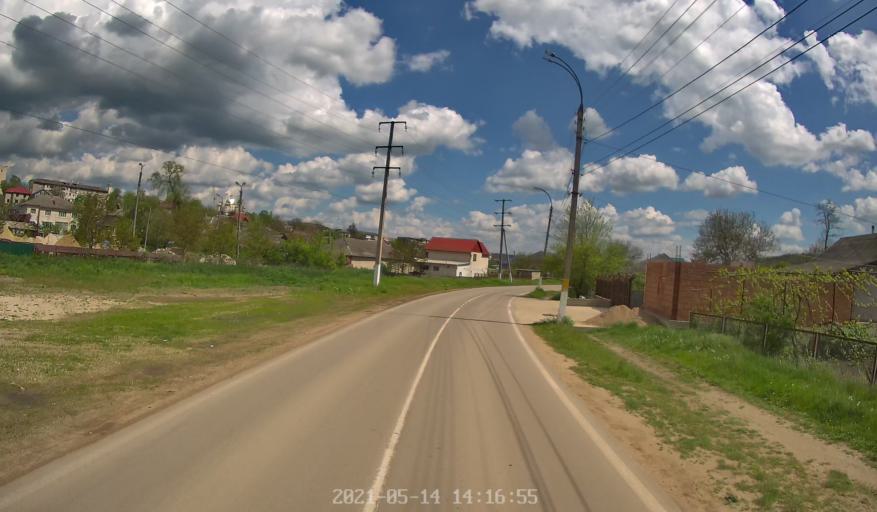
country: MD
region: Hincesti
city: Hincesti
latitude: 46.8243
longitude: 28.5895
